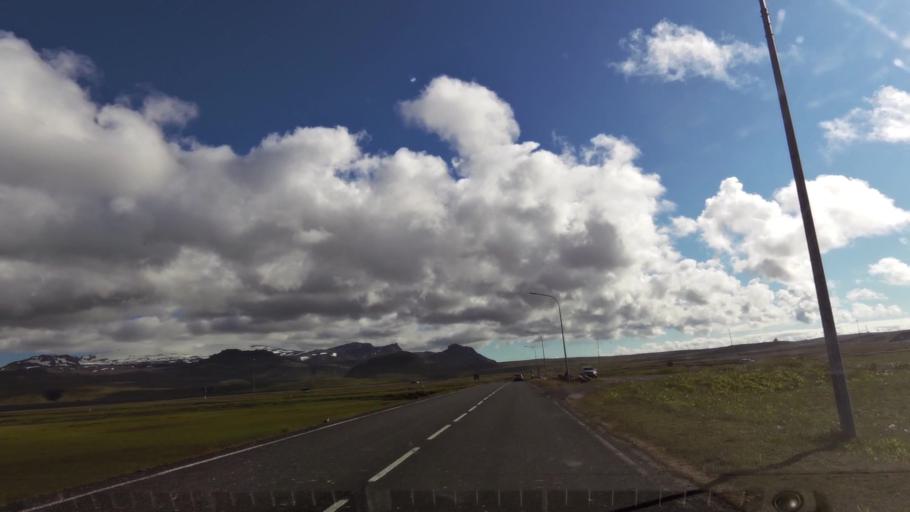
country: IS
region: West
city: Olafsvik
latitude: 64.9206
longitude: -23.8190
